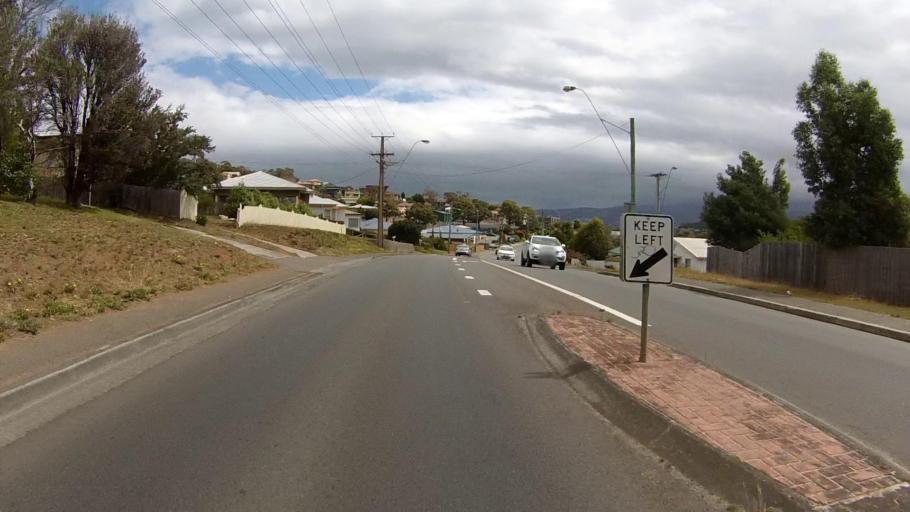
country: AU
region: Tasmania
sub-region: Clarence
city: Warrane
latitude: -42.8623
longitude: 147.3788
